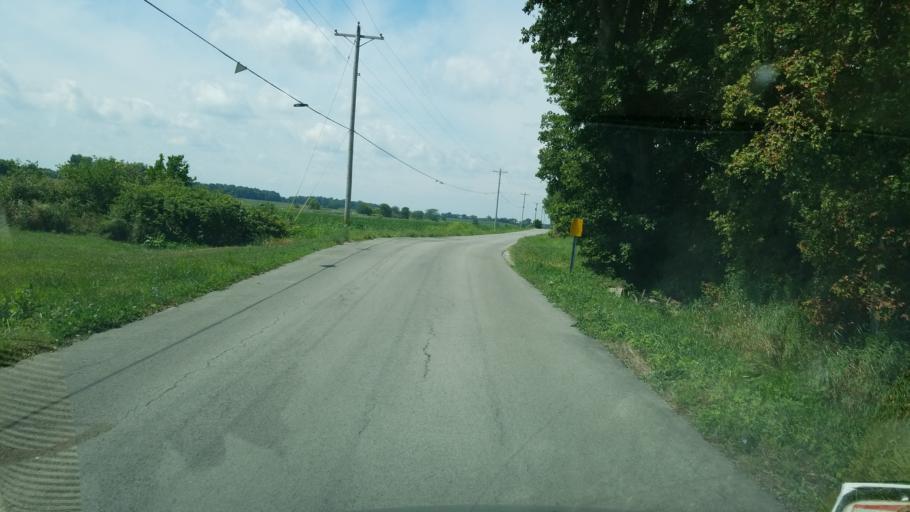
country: US
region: Ohio
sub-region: Hardin County
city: Forest
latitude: 40.8725
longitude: -83.5183
